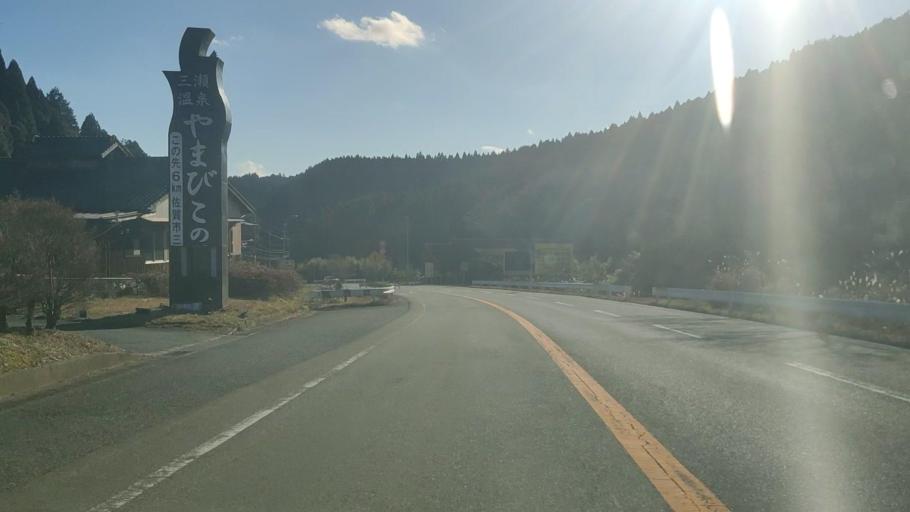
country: JP
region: Fukuoka
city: Maebaru-chuo
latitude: 33.4600
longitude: 130.2740
